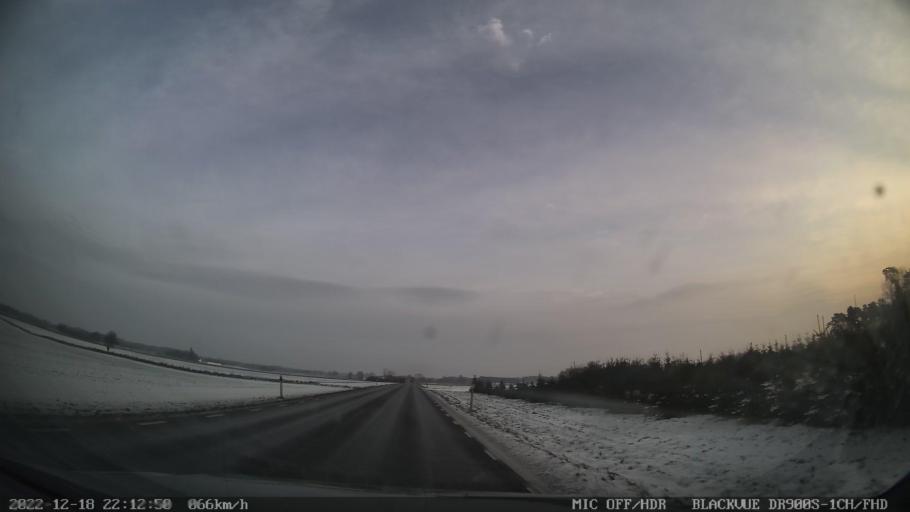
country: SE
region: Skane
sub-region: Tomelilla Kommun
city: Tomelilla
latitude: 55.5473
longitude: 14.0599
